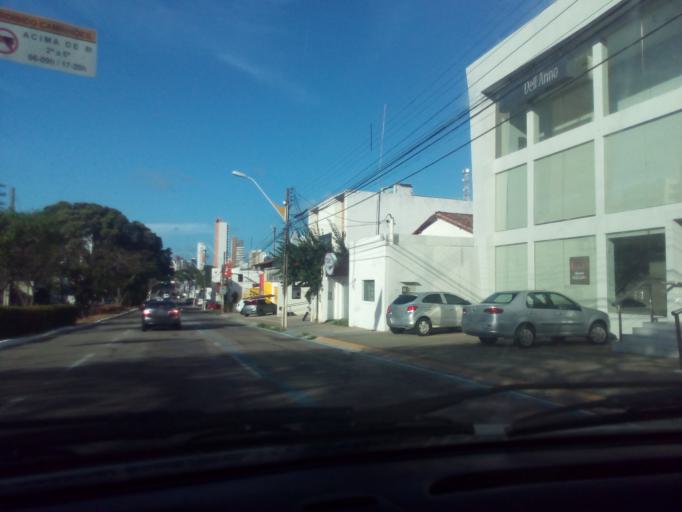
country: BR
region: Rio Grande do Norte
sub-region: Natal
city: Natal
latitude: -5.7986
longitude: -35.1999
